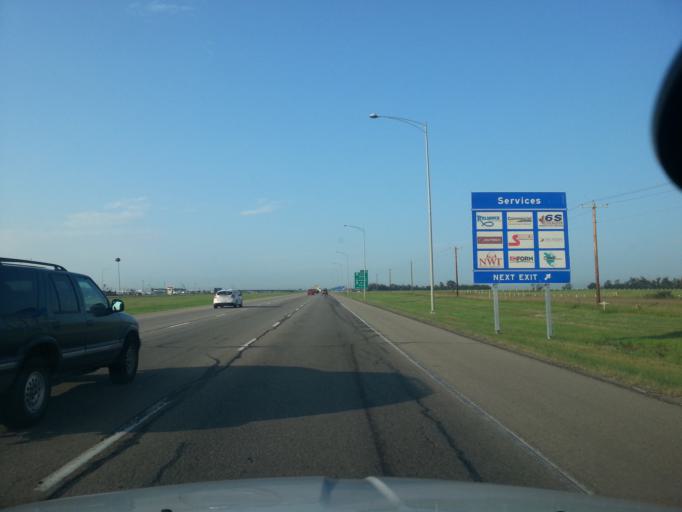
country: CA
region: Alberta
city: Leduc
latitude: 53.3520
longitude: -113.5418
